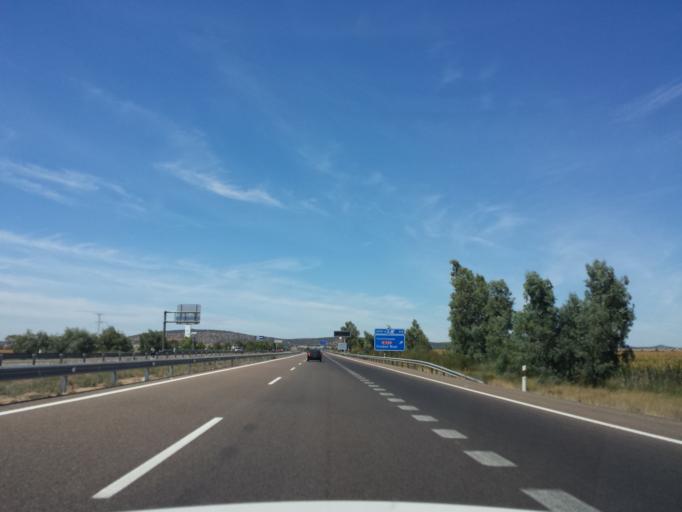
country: ES
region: Extremadura
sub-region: Provincia de Badajoz
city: Valdetorres
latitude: 38.9913
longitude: -6.1058
